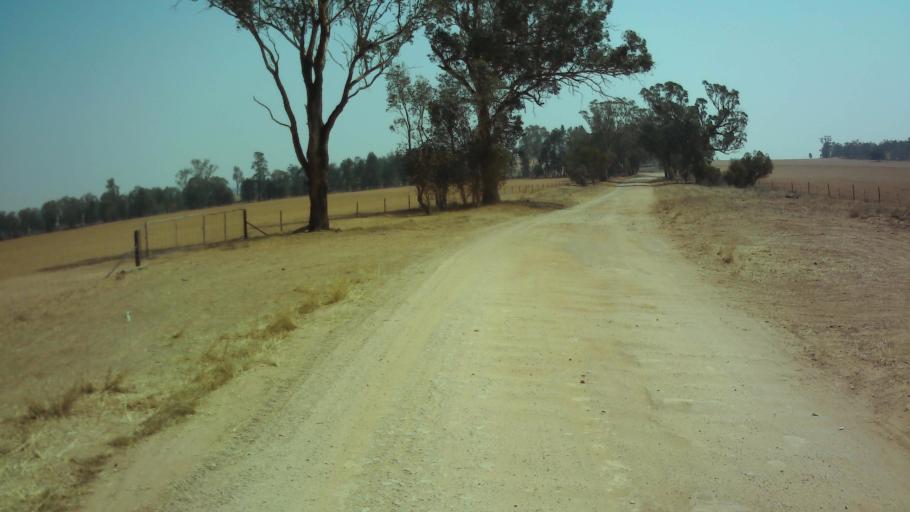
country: AU
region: New South Wales
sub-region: Weddin
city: Grenfell
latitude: -33.6491
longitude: 148.2700
